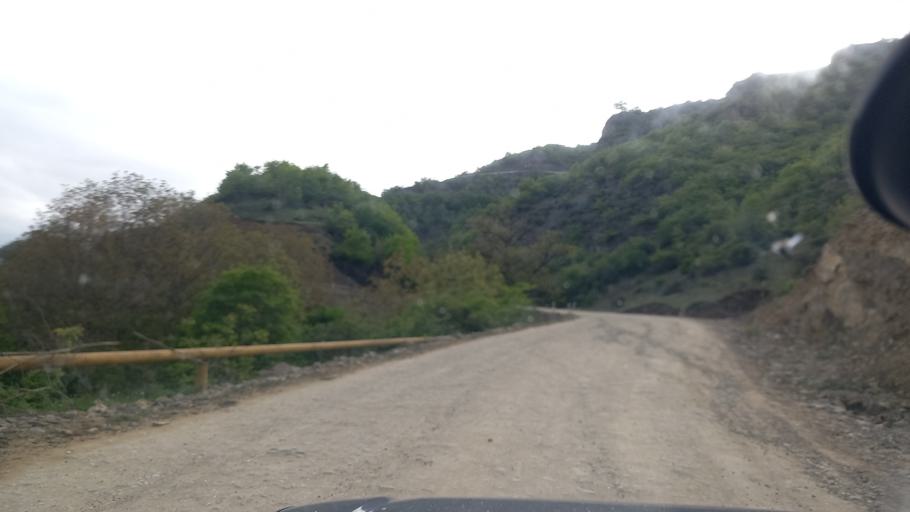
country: RU
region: Dagestan
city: Khuchni
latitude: 41.9684
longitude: 47.8757
